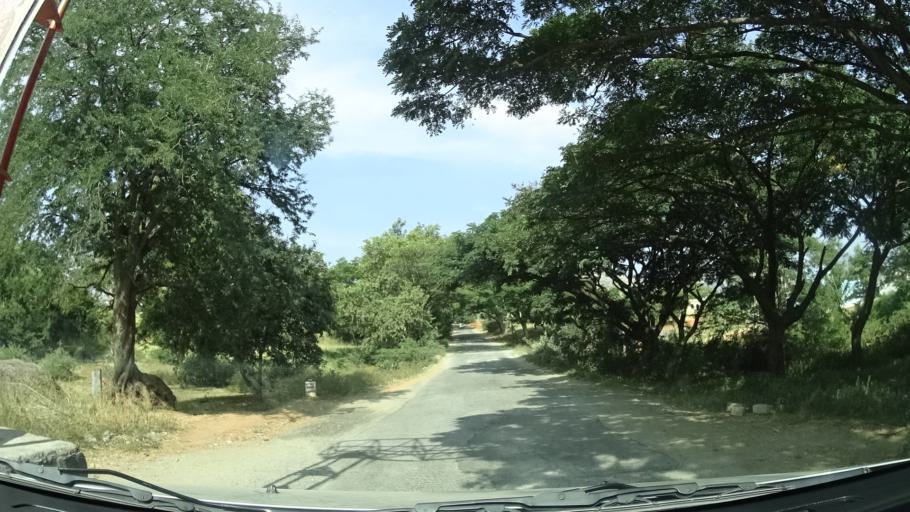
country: IN
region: Karnataka
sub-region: Chikkaballapur
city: Chik Ballapur
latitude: 13.4020
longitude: 77.7082
